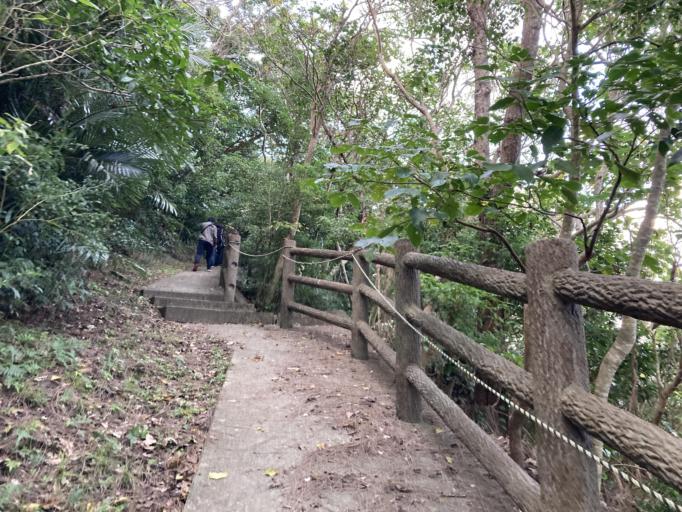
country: JP
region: Okinawa
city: Nago
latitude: 26.8585
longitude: 128.2610
